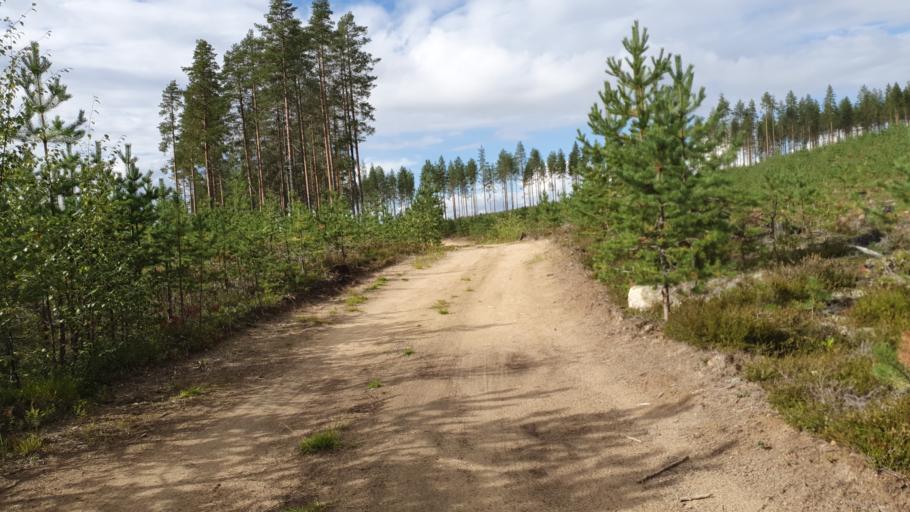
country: FI
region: Kainuu
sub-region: Kehys-Kainuu
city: Kuhmo
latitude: 64.1481
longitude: 29.3784
